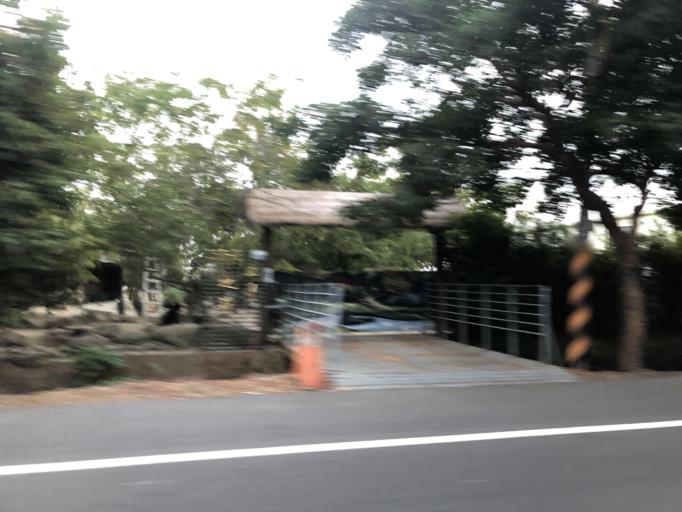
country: TW
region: Taiwan
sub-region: Tainan
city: Tainan
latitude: 23.0233
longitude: 120.3066
